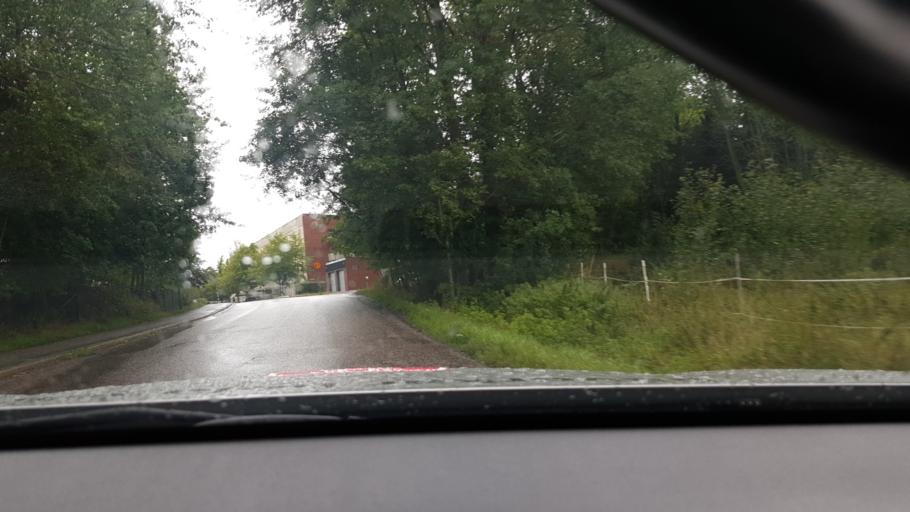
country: SE
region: Stockholm
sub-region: Haninge Kommun
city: Jordbro
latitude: 59.0999
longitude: 18.0441
